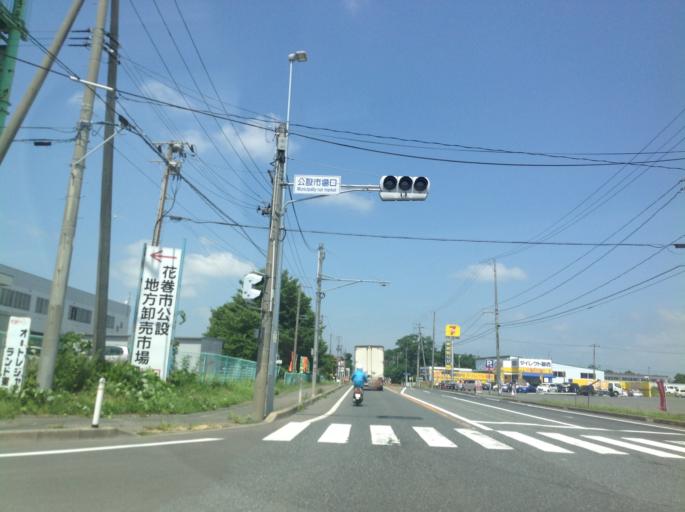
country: JP
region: Iwate
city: Hanamaki
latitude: 39.3563
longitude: 141.1116
